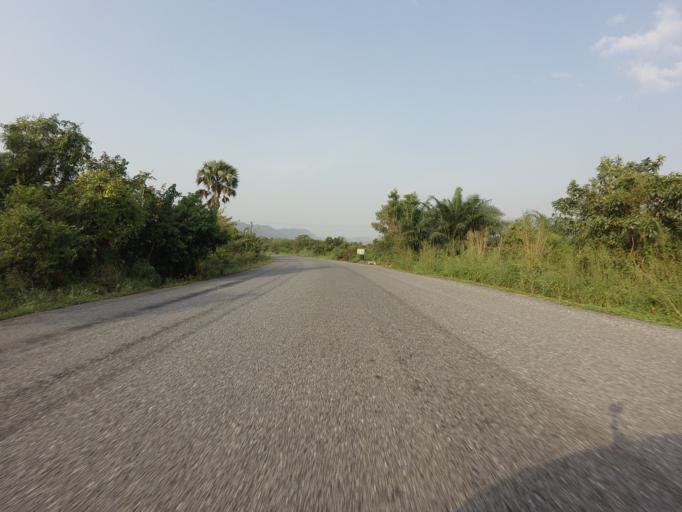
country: GH
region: Volta
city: Ho
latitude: 6.4248
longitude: 0.1902
